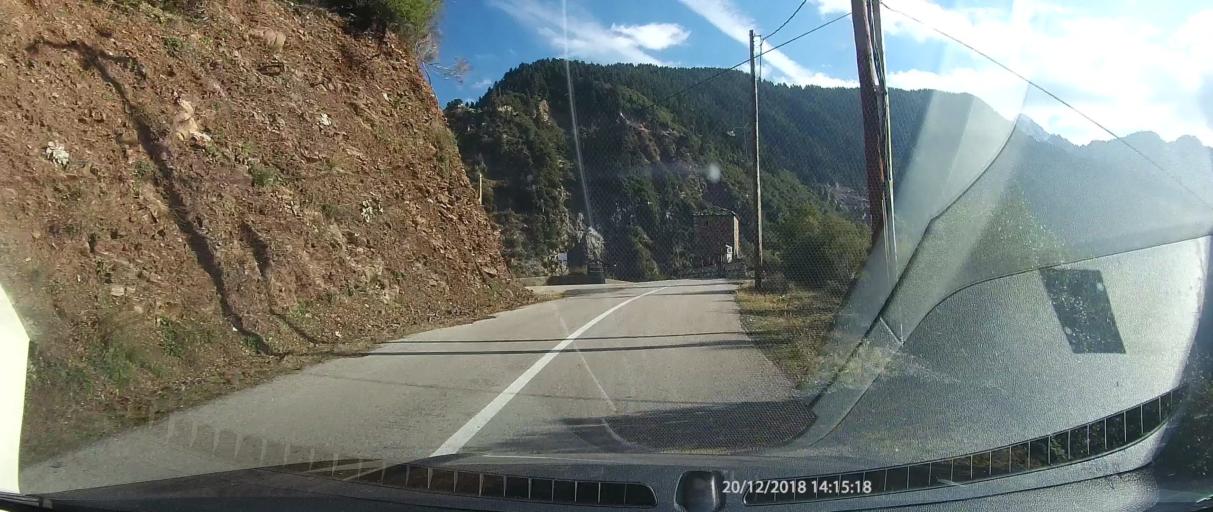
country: GR
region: West Greece
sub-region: Nomos Aitolias kai Akarnanias
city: Thermo
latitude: 38.7500
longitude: 21.6561
